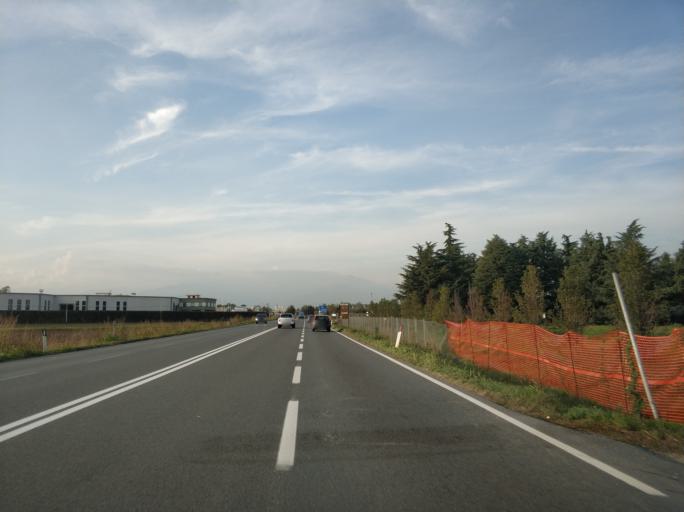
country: IT
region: Piedmont
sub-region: Provincia di Torino
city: San Maurizio
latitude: 45.2126
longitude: 7.6144
